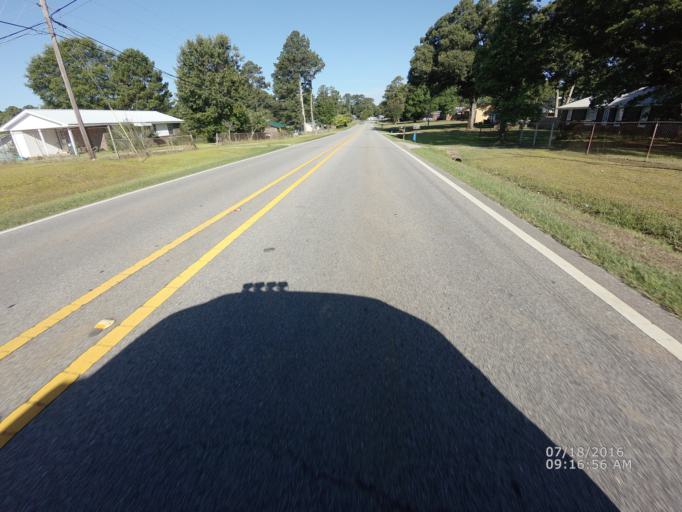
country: US
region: Alabama
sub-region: Chambers County
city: Huguley
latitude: 32.8520
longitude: -85.2698
